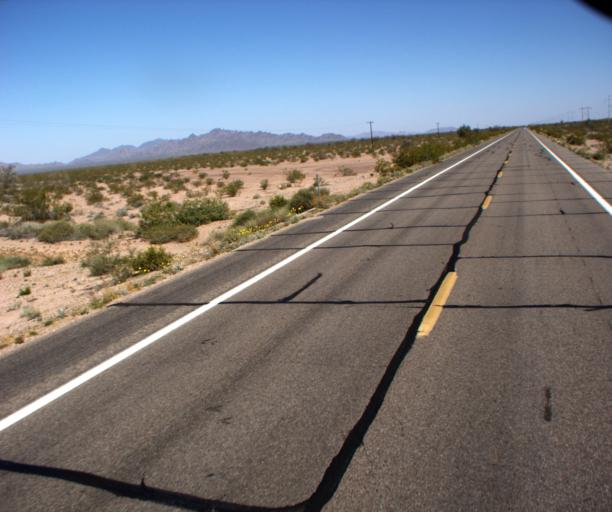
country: US
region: Arizona
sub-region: La Paz County
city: Quartzsite
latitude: 33.3999
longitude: -114.2172
